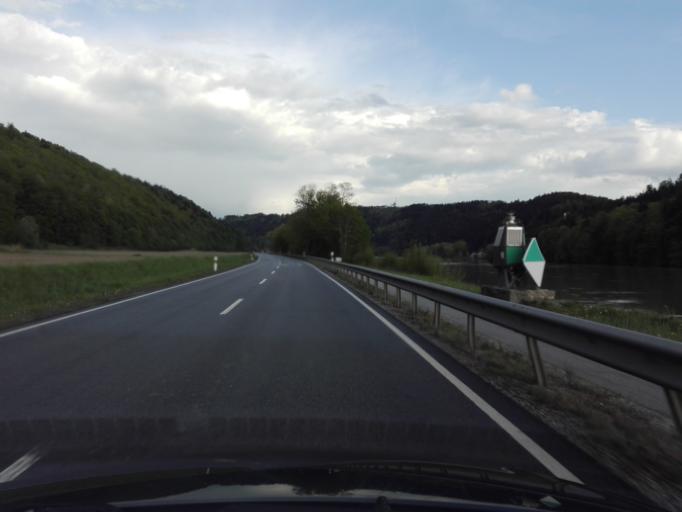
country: DE
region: Bavaria
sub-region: Lower Bavaria
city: Thyrnau
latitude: 48.5689
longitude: 13.5554
